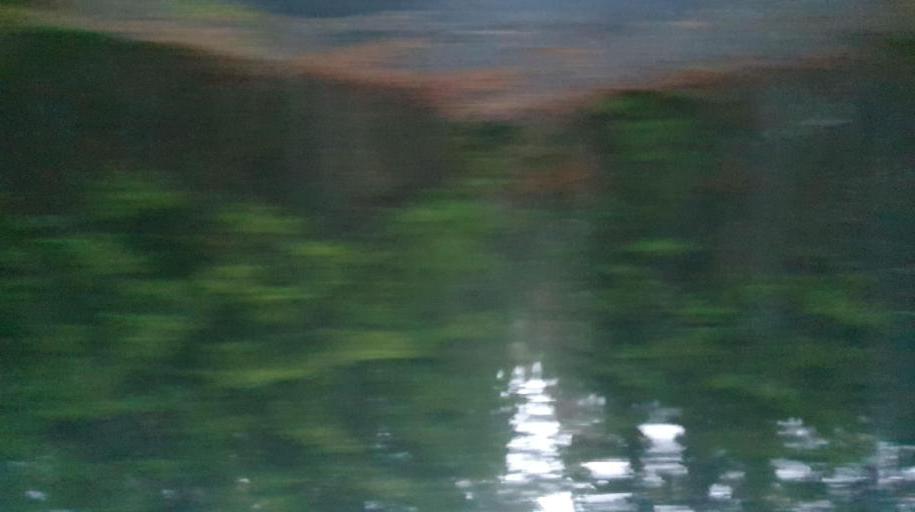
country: NO
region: Buskerud
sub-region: Krodsherad
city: Noresund
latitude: 60.1469
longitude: 9.7639
